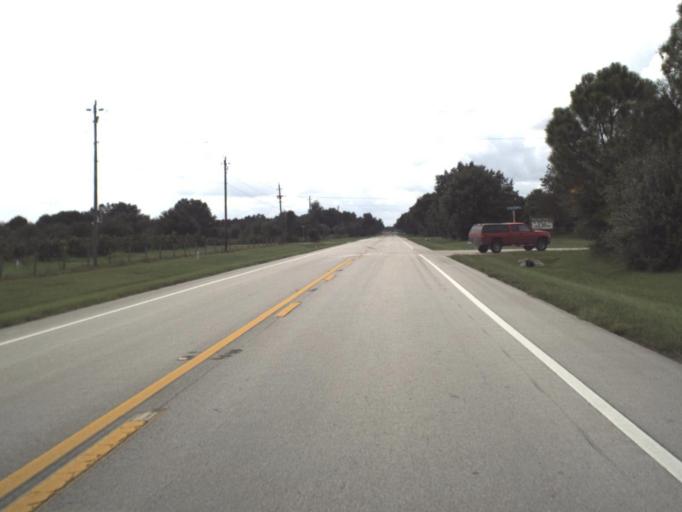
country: US
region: Florida
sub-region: DeSoto County
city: Nocatee
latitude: 27.2016
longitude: -81.9470
